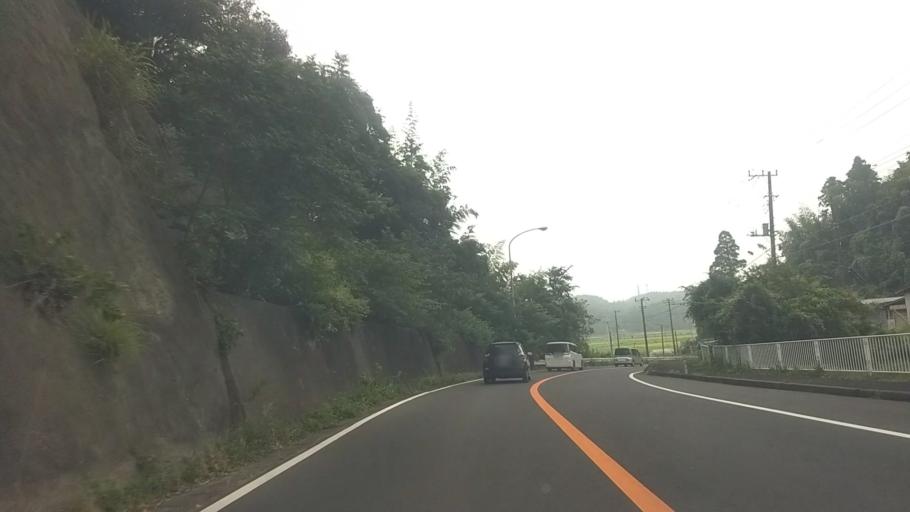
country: JP
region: Chiba
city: Ohara
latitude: 35.2653
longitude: 140.3715
